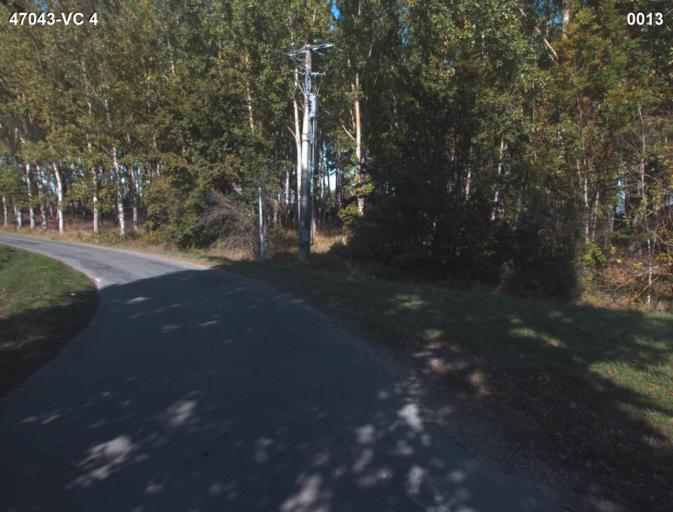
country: FR
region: Aquitaine
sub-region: Departement du Lot-et-Garonne
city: Buzet-sur-Baise
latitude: 44.2590
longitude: 0.3074
